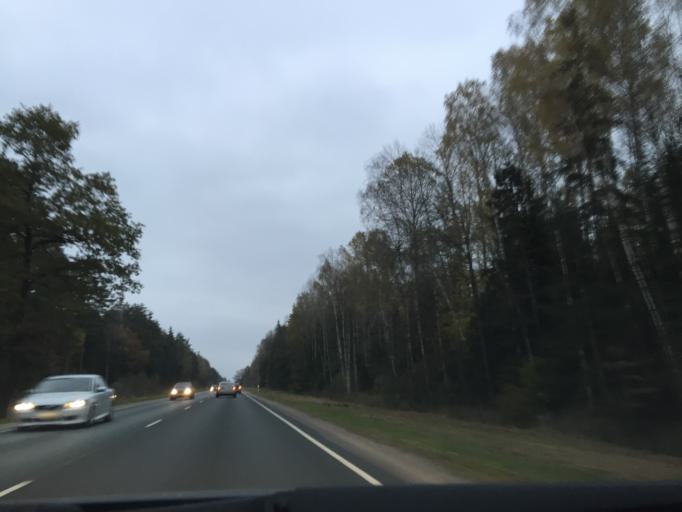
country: LV
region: Ozolnieku
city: Ozolnieki
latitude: 56.7082
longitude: 23.8240
